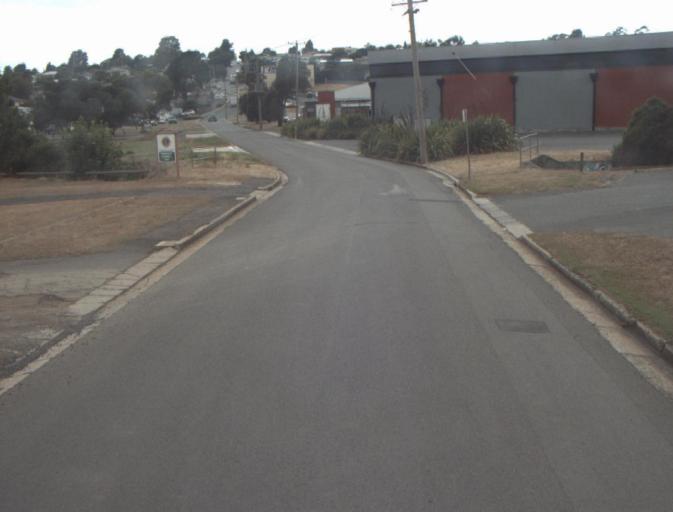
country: AU
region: Tasmania
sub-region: Launceston
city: Summerhill
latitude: -41.4767
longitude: 147.1610
